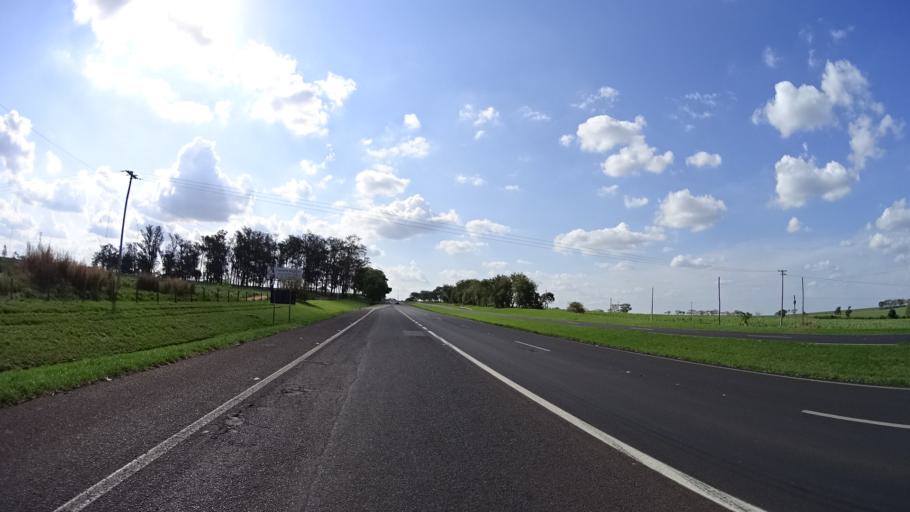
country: BR
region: Sao Paulo
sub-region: Guapiacu
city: Guapiacu
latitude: -20.9896
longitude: -49.2074
